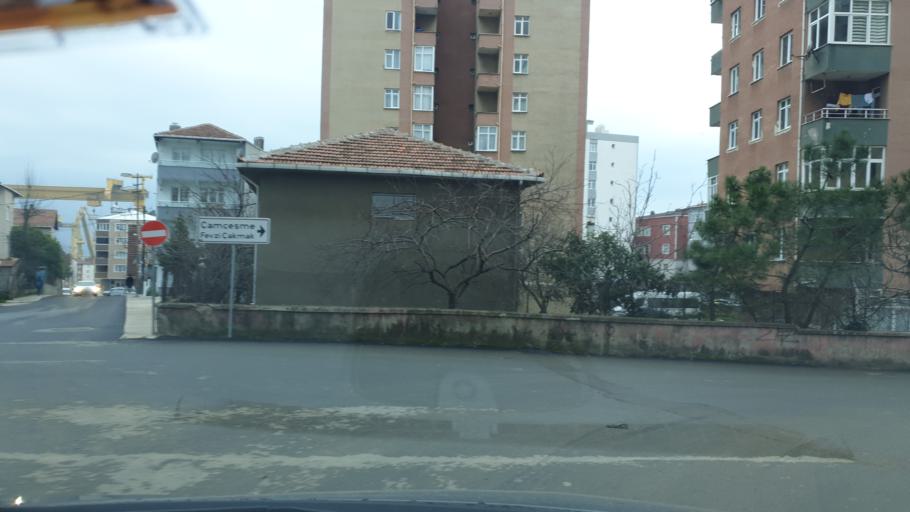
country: TR
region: Istanbul
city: Pendik
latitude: 40.8708
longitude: 29.2665
